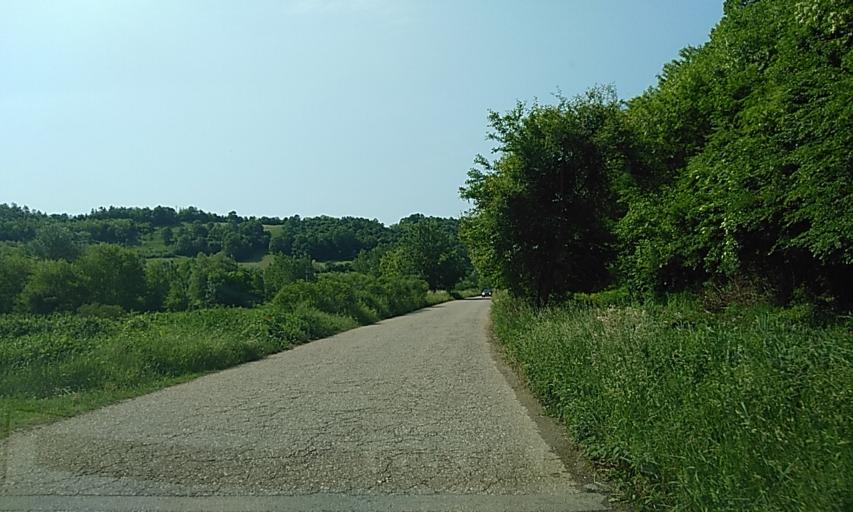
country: RS
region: Central Serbia
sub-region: Pcinjski Okrug
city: Vladicin Han
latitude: 42.7309
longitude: 22.0634
